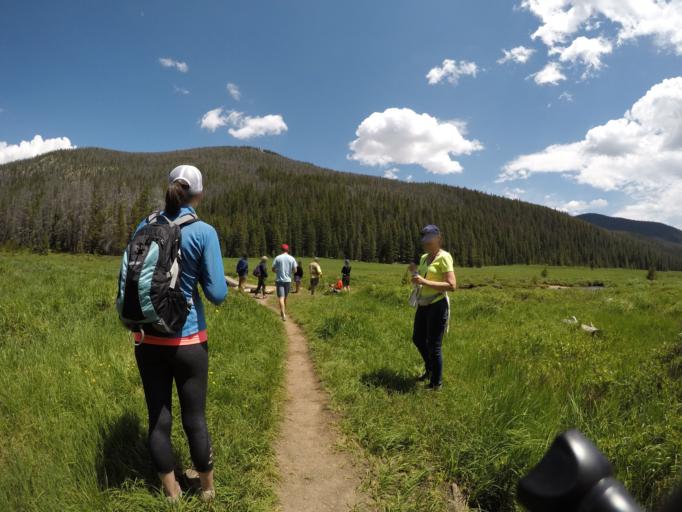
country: US
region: Colorado
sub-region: Grand County
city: Granby
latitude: 40.3098
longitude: -105.8100
